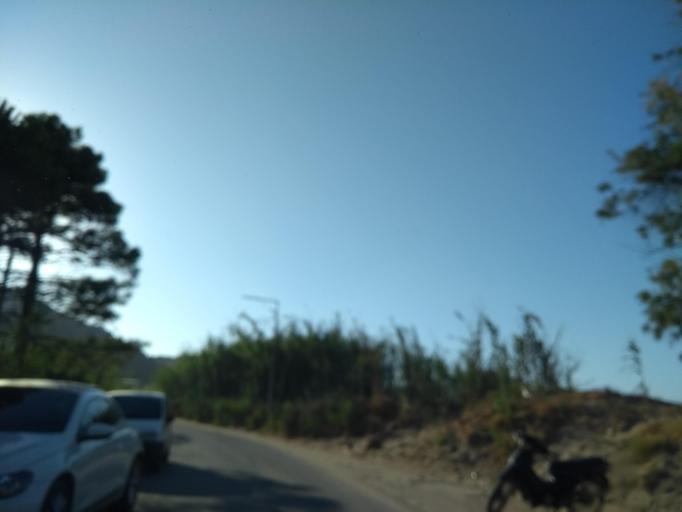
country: GR
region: Crete
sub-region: Nomos Chanias
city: Kalivai
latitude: 35.4639
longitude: 24.1578
